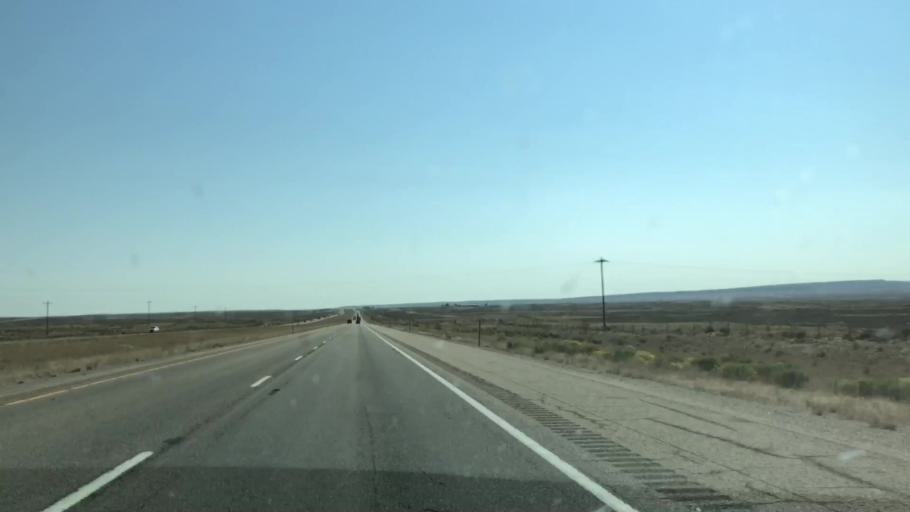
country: US
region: Wyoming
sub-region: Sweetwater County
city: Rock Springs
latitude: 41.6373
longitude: -108.4483
